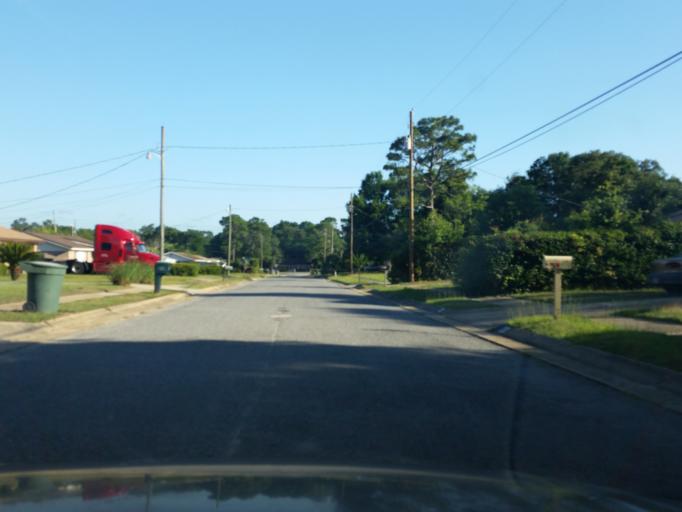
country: US
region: Florida
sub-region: Escambia County
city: Ferry Pass
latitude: 30.5188
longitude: -87.1835
